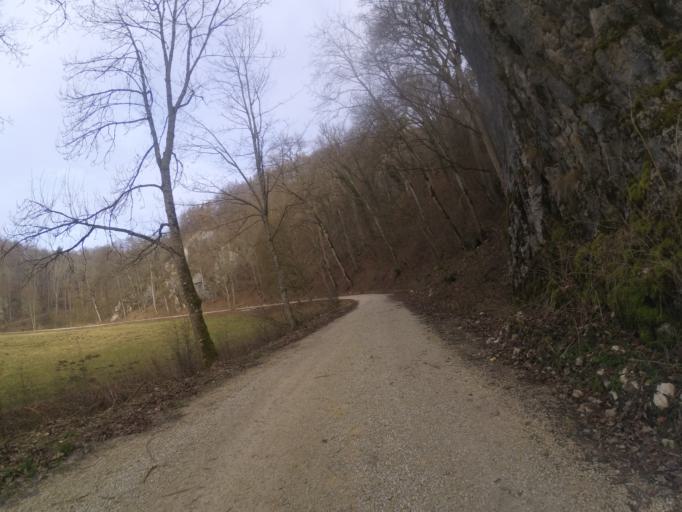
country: DE
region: Baden-Wuerttemberg
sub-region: Tuebingen Region
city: Rechtenstein
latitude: 48.2606
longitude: 9.5571
